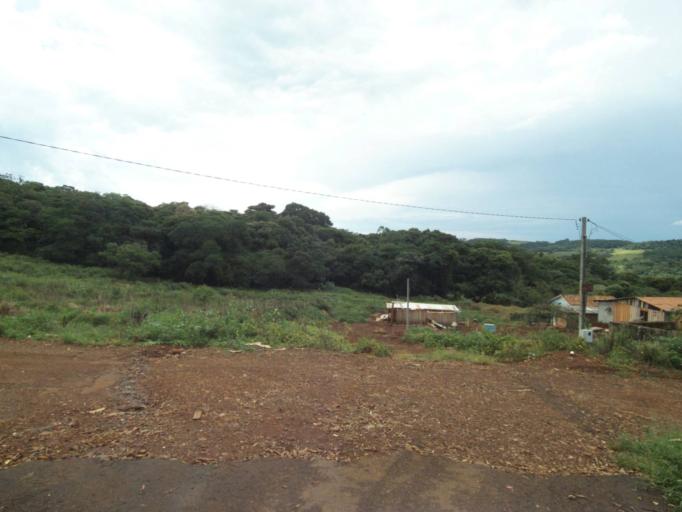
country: BR
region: Parana
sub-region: Guaraniacu
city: Guaraniacu
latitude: -25.0936
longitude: -52.8716
